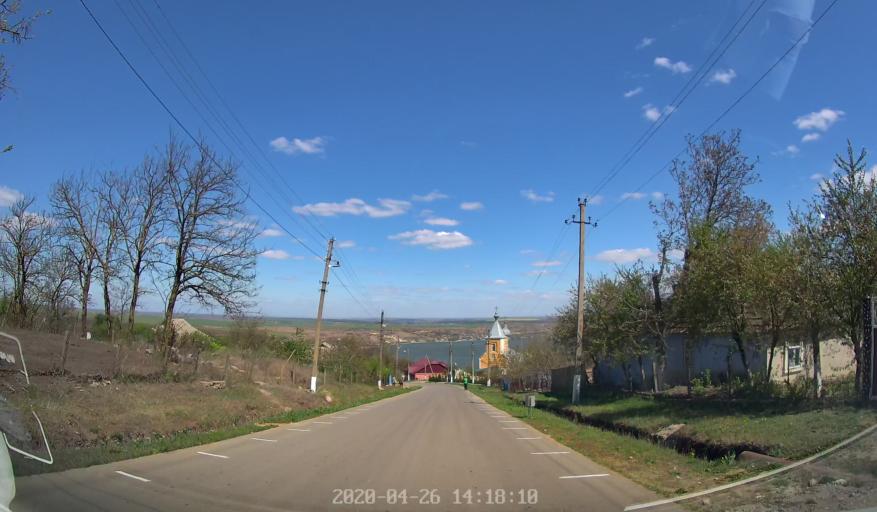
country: MD
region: Telenesti
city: Cocieri
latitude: 47.3543
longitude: 29.0573
